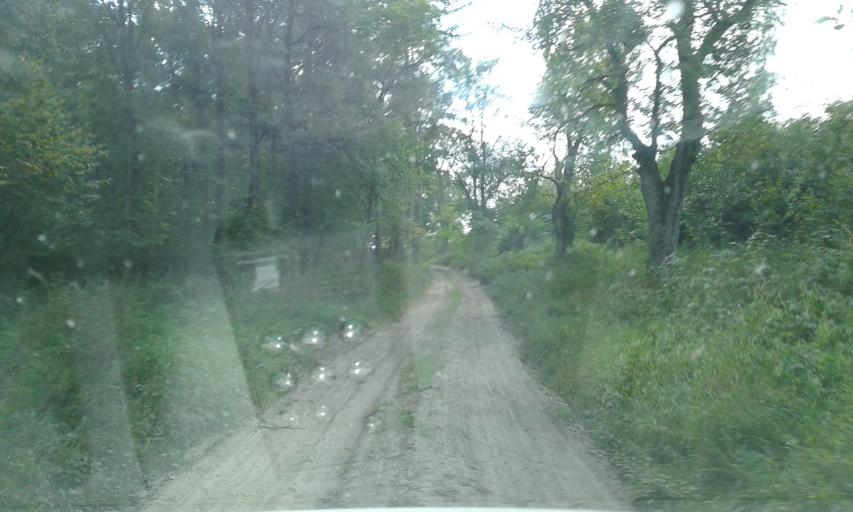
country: PL
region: West Pomeranian Voivodeship
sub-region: Powiat stargardzki
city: Dolice
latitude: 53.2500
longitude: 15.2163
